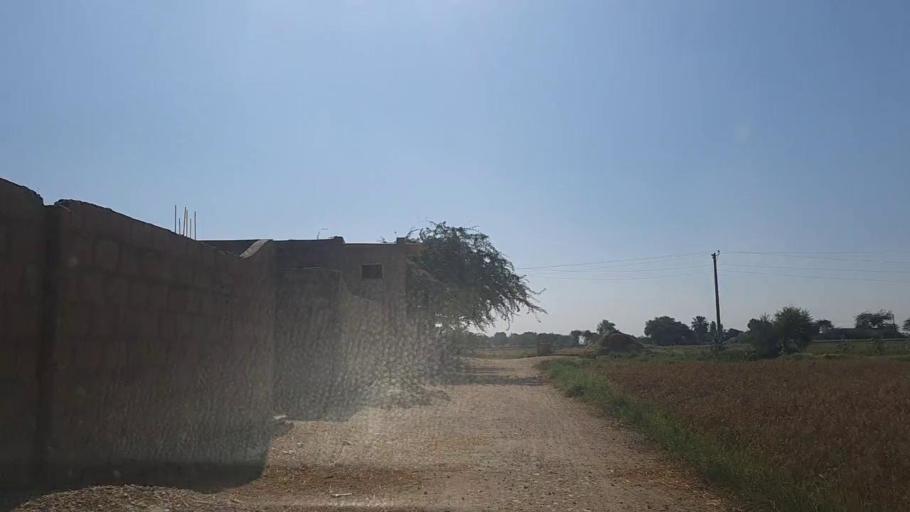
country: PK
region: Sindh
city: Thatta
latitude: 24.7717
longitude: 67.9484
